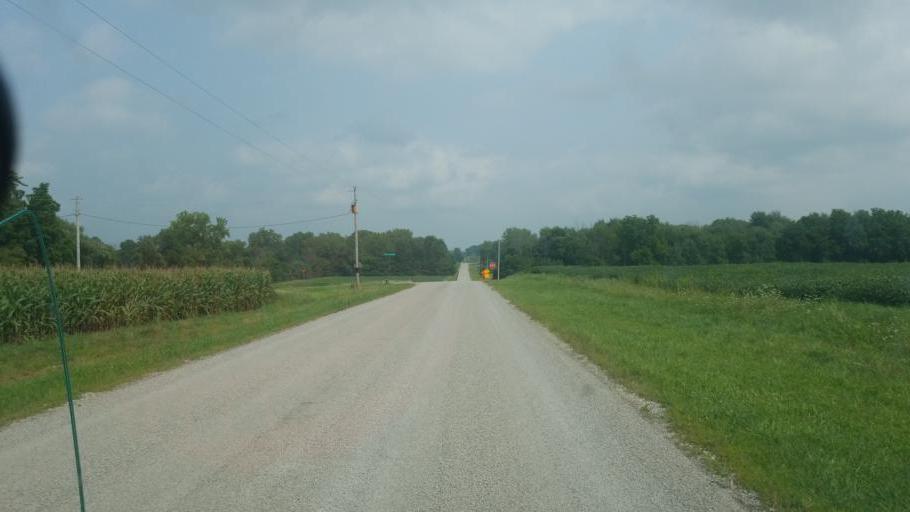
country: US
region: Ohio
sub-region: Huron County
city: Greenwich
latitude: 41.0667
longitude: -82.5447
